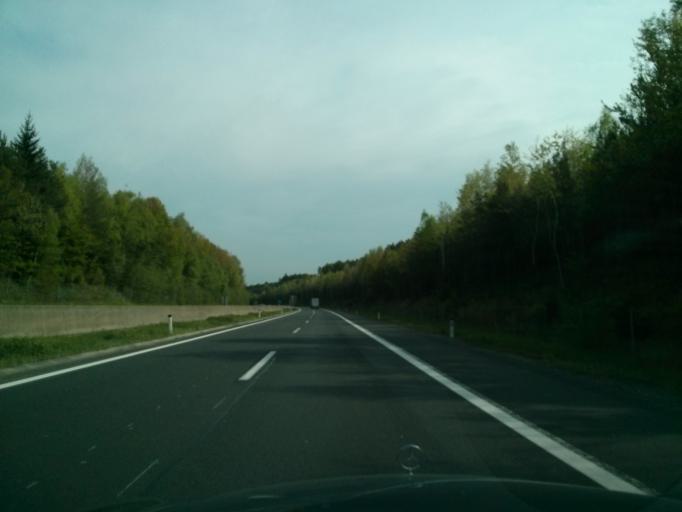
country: AT
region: Styria
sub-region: Politischer Bezirk Hartberg-Fuerstenfeld
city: Bad Waltersdorf
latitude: 47.1493
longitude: 15.9969
